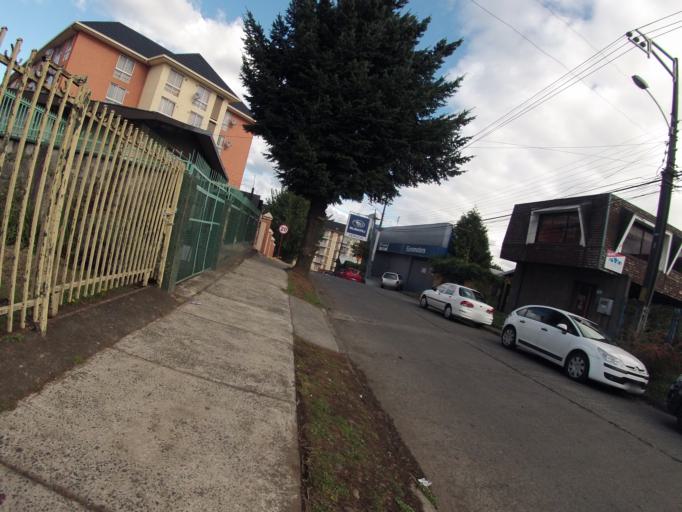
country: CL
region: Araucania
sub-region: Provincia de Cautin
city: Temuco
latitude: -38.7432
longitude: -72.5970
